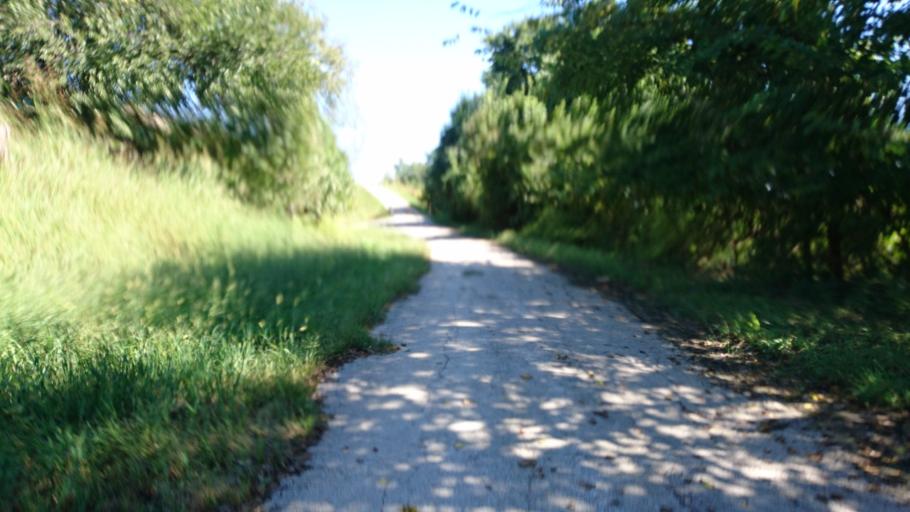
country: US
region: Illinois
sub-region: Madison County
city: East Alton
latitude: 38.8619
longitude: -90.1327
